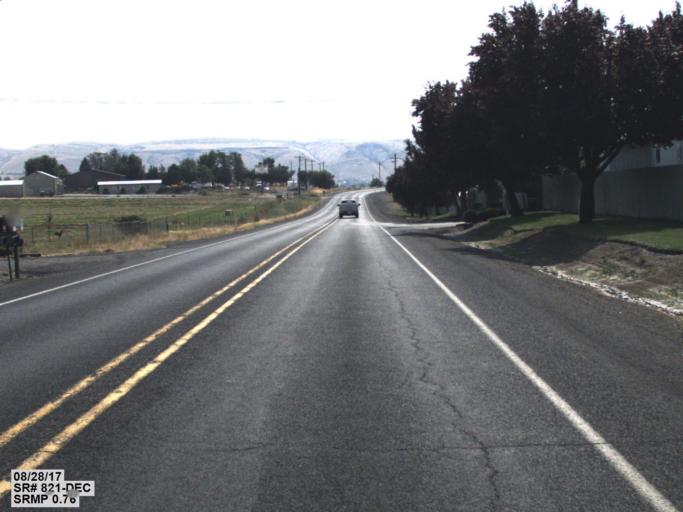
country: US
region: Washington
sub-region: Yakima County
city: Selah
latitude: 46.6869
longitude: -120.4779
